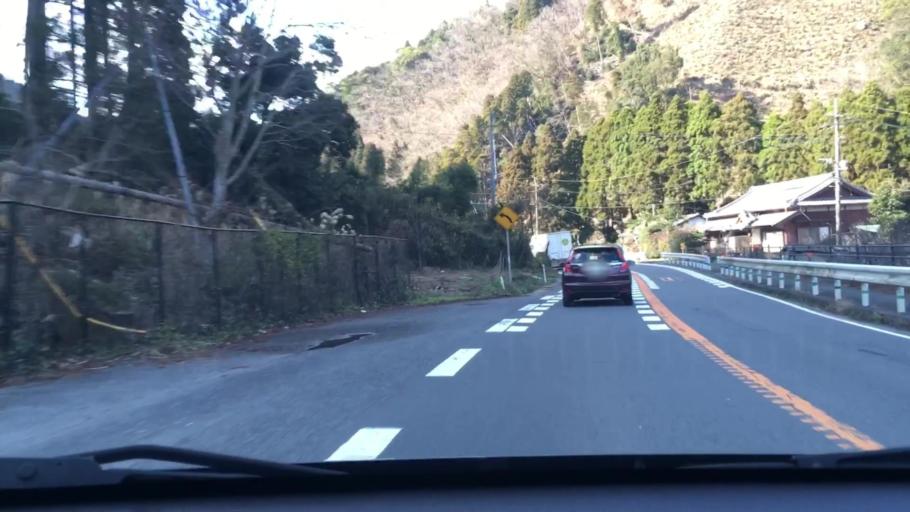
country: JP
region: Oita
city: Tsukumiura
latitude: 33.0007
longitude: 131.8093
